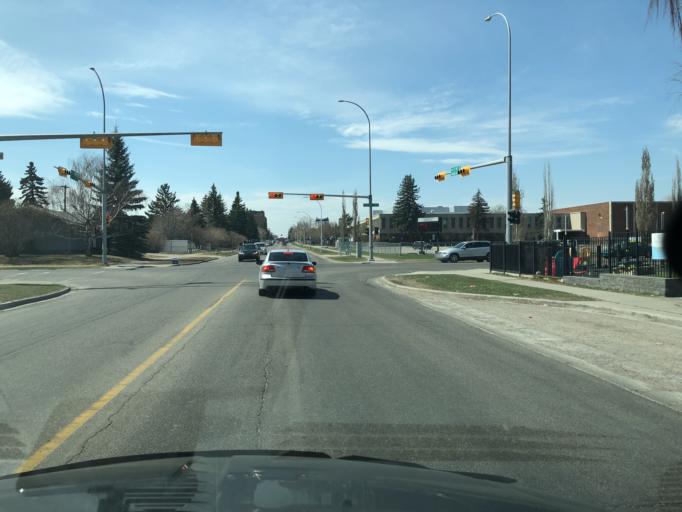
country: CA
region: Alberta
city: Calgary
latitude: 50.9722
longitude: -114.0585
